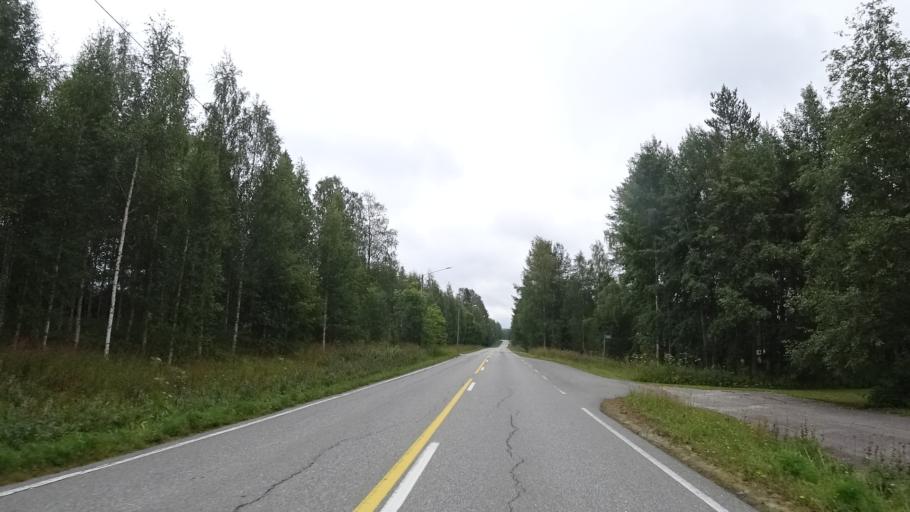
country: FI
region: North Karelia
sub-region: Pielisen Karjala
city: Lieksa
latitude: 63.2837
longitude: 30.5320
